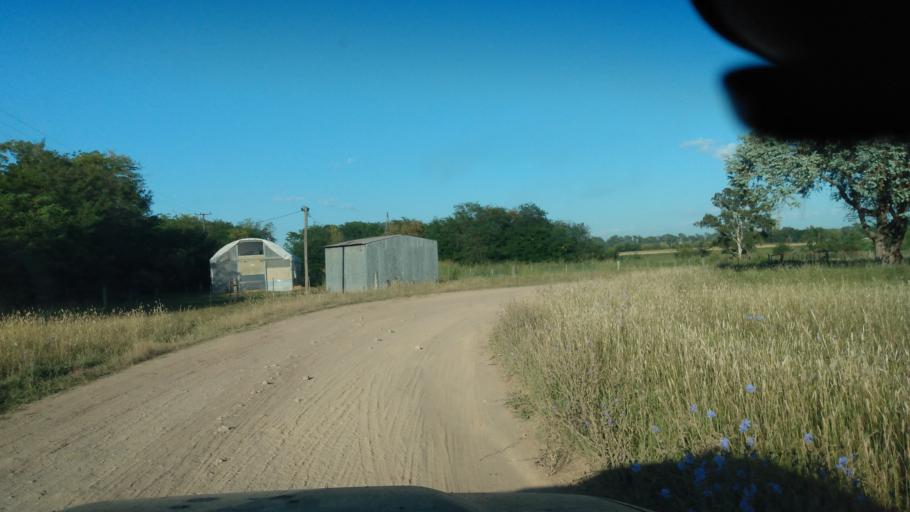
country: AR
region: Buenos Aires
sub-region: Partido de Lujan
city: Lujan
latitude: -34.5894
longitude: -59.0626
